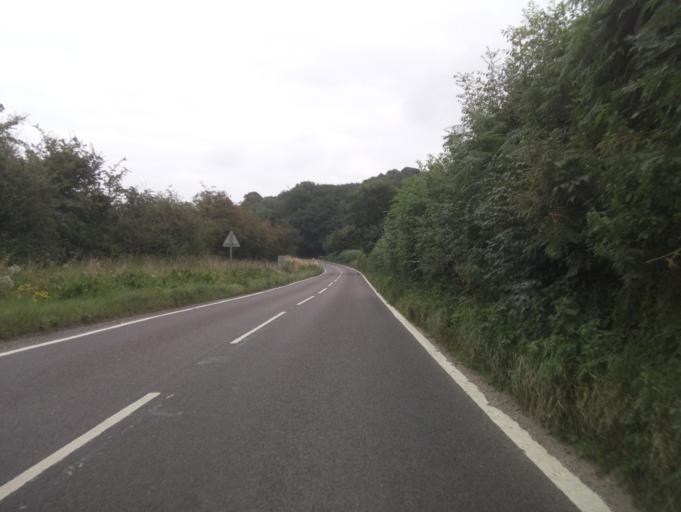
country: GB
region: England
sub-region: Derbyshire
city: Ashbourne
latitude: 53.0133
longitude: -1.7100
